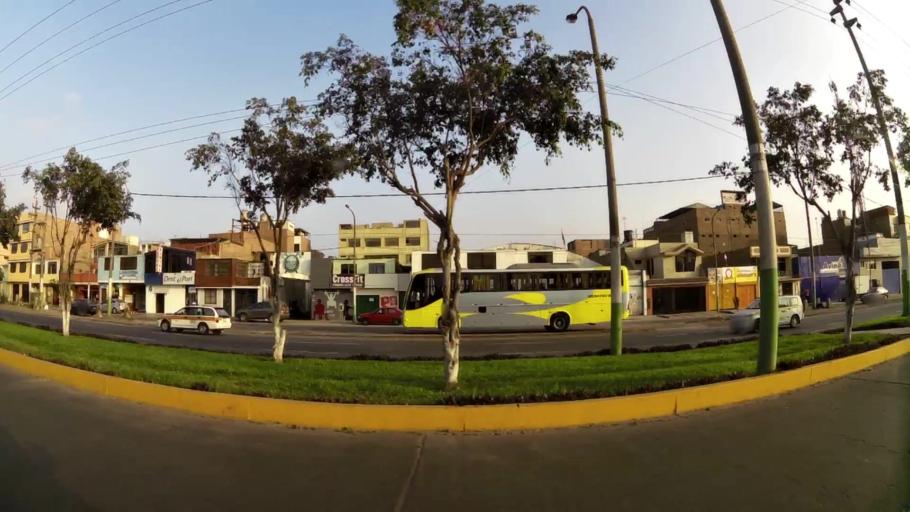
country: PE
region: Lima
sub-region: Lima
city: Independencia
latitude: -11.9916
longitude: -77.0785
